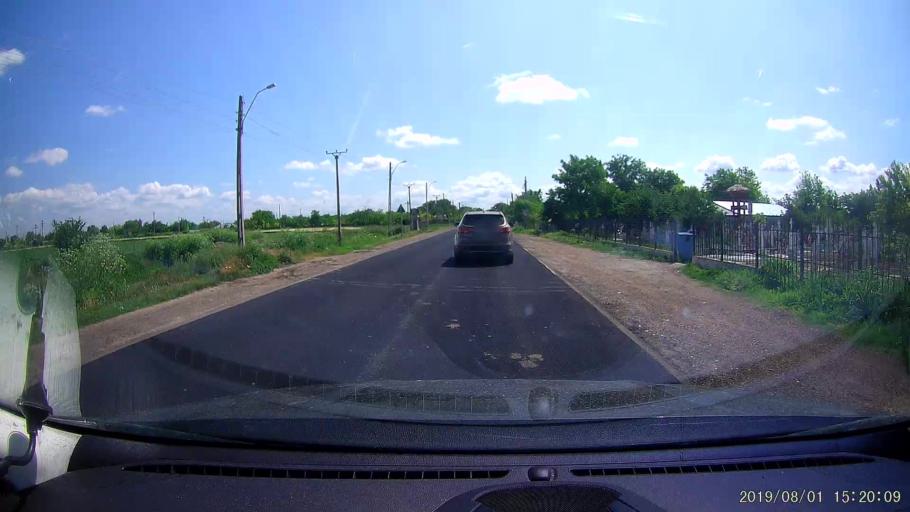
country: RO
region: Braila
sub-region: Comuna Tufesti
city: Tufesti
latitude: 45.0817
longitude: 27.8086
